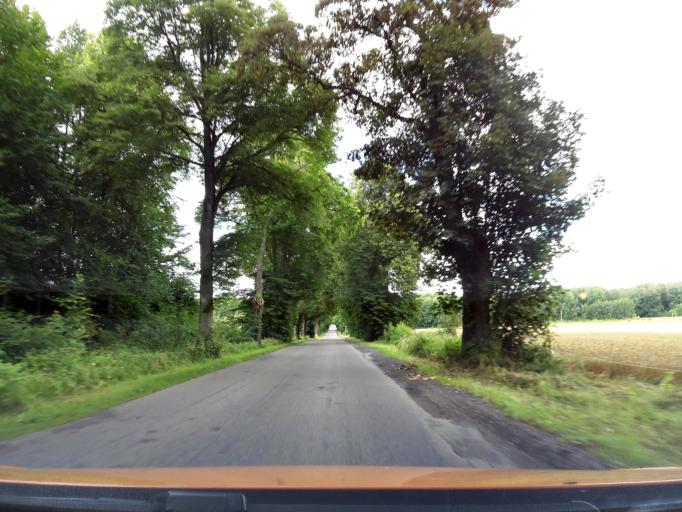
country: PL
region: West Pomeranian Voivodeship
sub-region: Powiat kolobrzeski
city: Ryman
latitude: 53.9594
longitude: 15.4928
